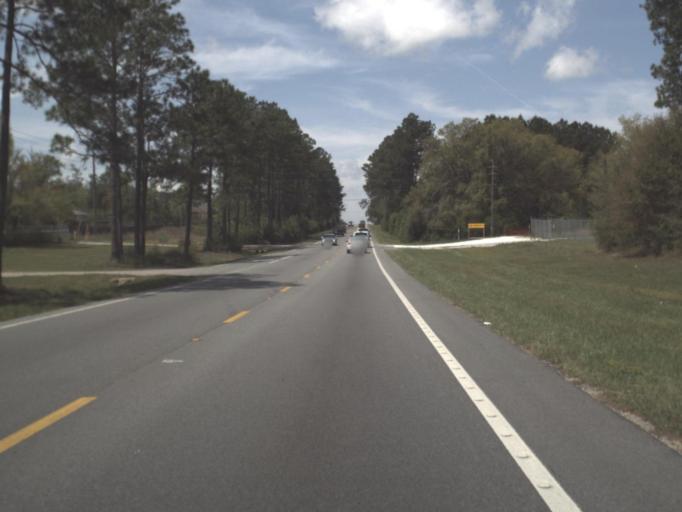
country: US
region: Florida
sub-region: Escambia County
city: Gonzalez
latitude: 30.5349
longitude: -87.3454
